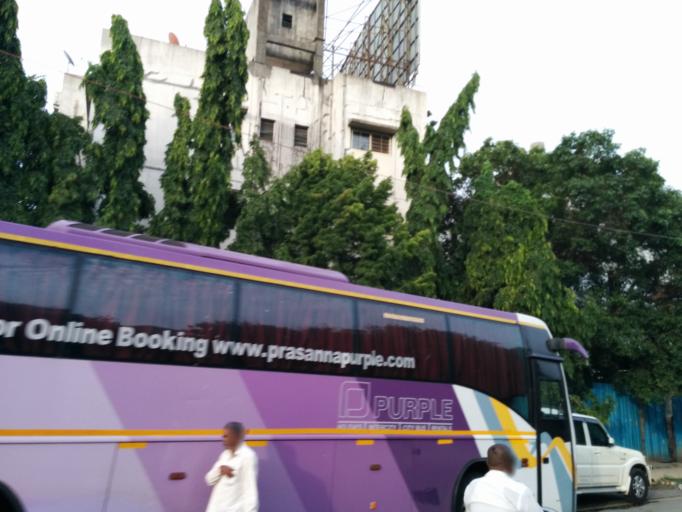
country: IN
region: Maharashtra
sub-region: Pune Division
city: Pune
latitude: 18.5095
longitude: 73.8215
